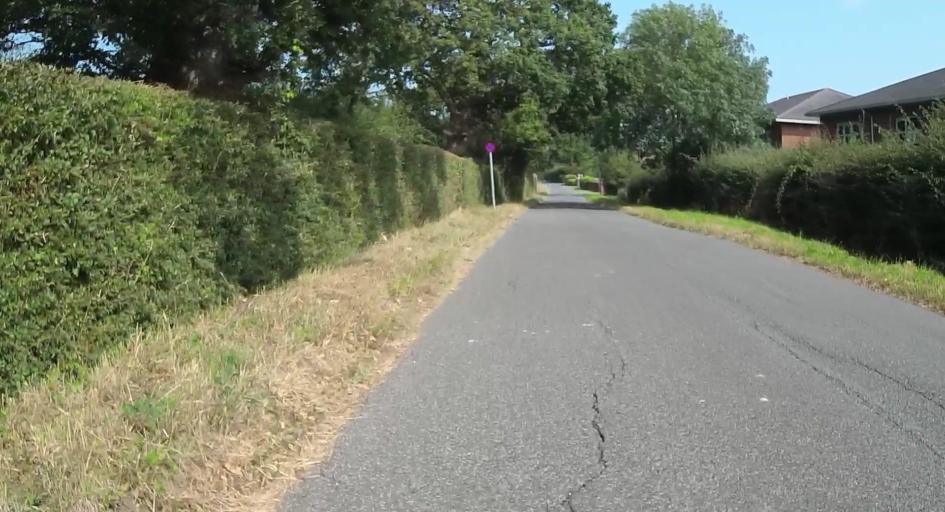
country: GB
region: England
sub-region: Isle of Wight
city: Newport
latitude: 50.7133
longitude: -1.2964
